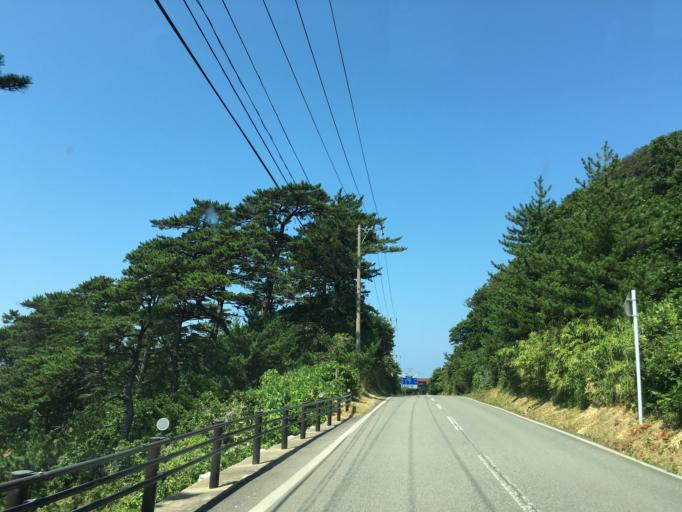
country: JP
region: Akita
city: Tenno
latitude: 39.9093
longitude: 139.7253
